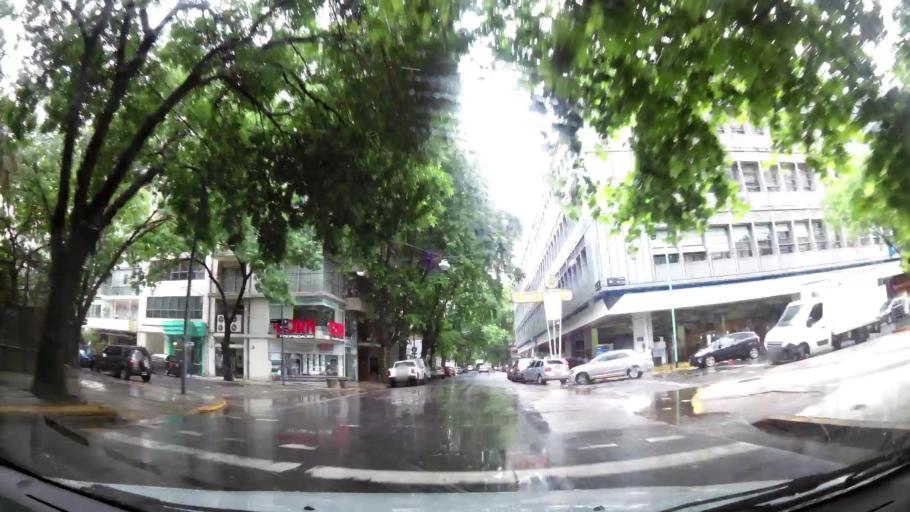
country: AR
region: Buenos Aires F.D.
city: Colegiales
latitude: -34.5746
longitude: -58.4218
